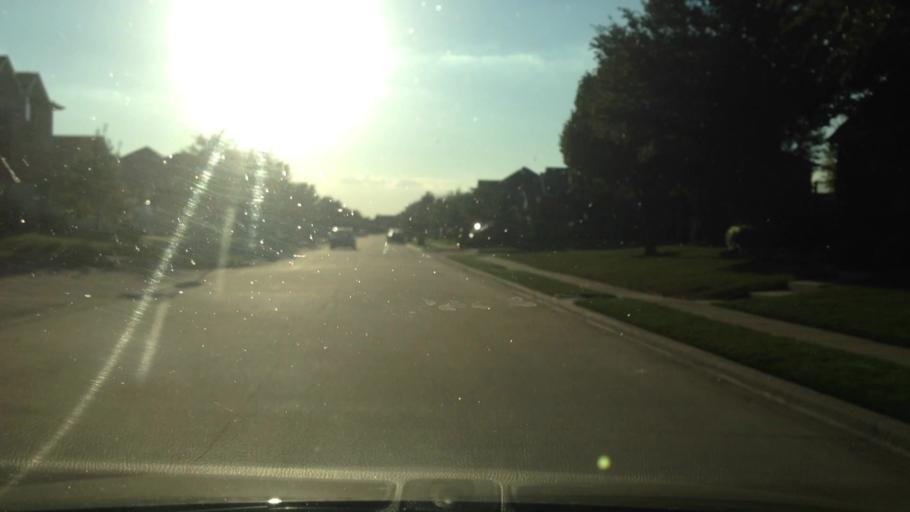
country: US
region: Texas
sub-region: Denton County
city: Little Elm
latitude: 33.1416
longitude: -96.9177
